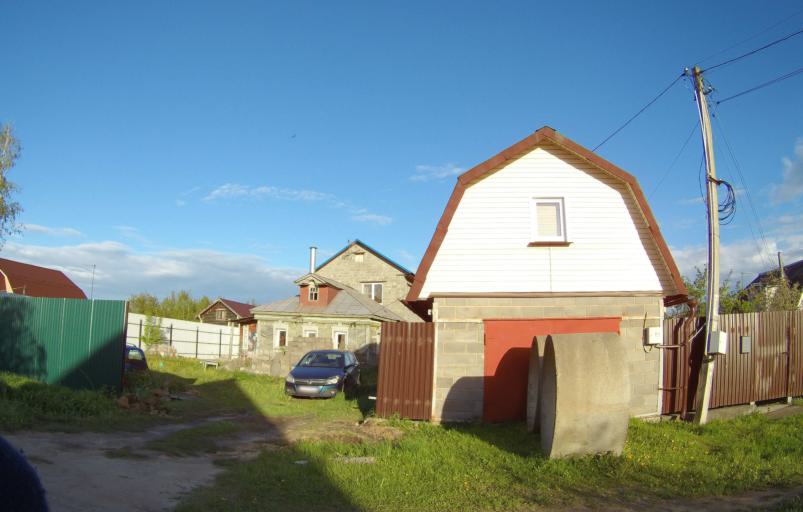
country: RU
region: Moskovskaya
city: Ramenskoye
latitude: 55.5875
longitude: 38.2647
